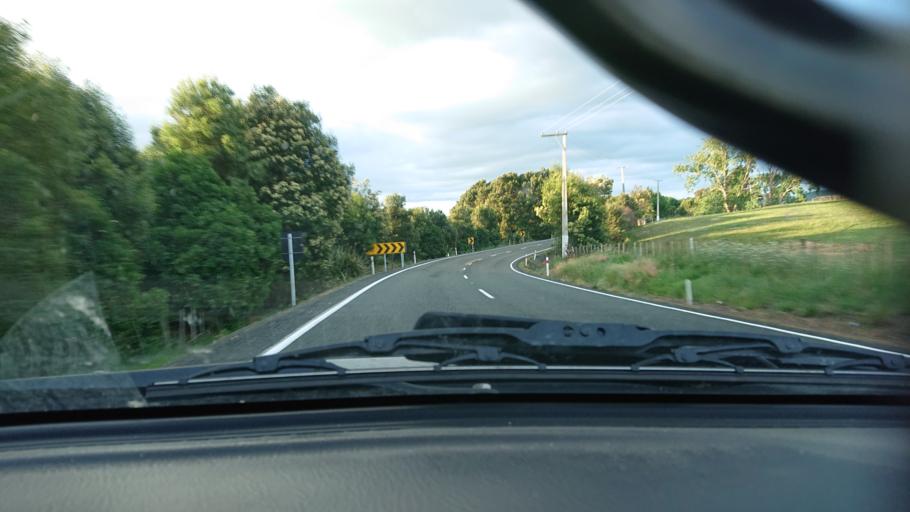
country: NZ
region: Auckland
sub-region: Auckland
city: Parakai
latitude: -36.5220
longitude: 174.4489
